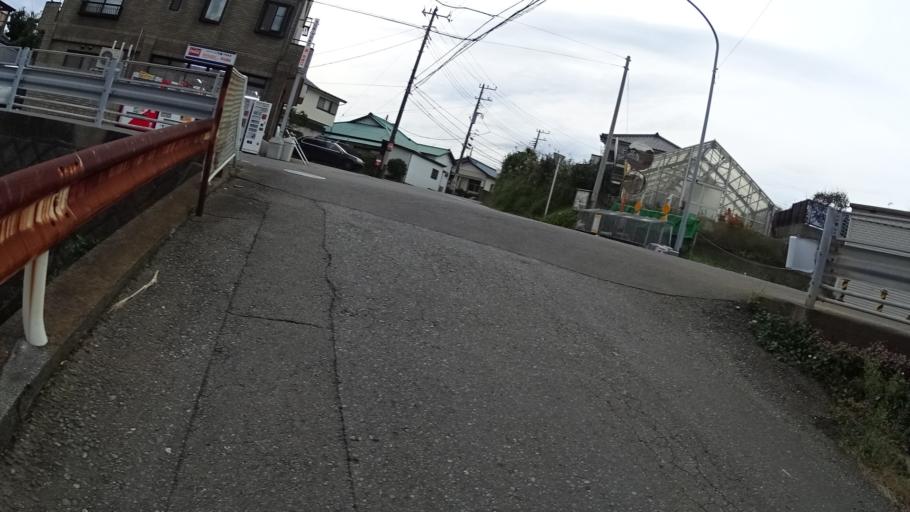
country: JP
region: Kanagawa
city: Miura
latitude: 35.1438
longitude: 139.6349
